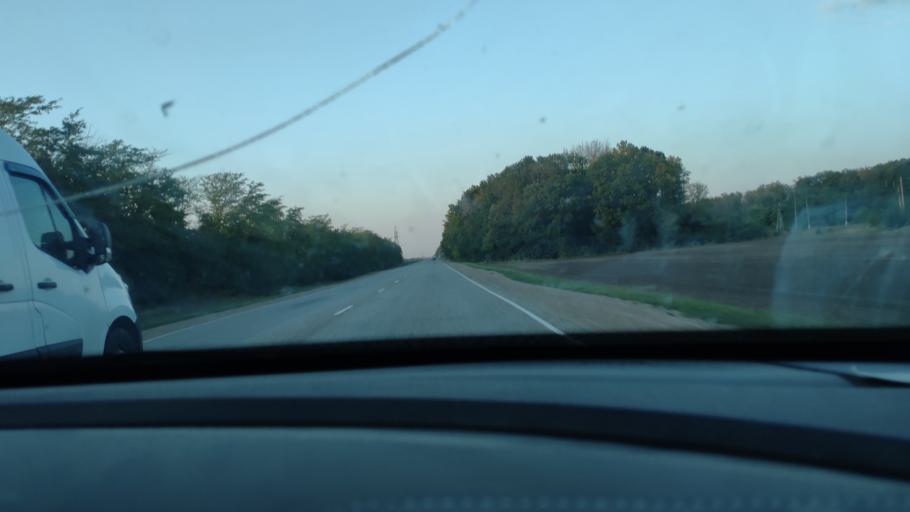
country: RU
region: Krasnodarskiy
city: Starominskaya
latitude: 46.4839
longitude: 39.0537
